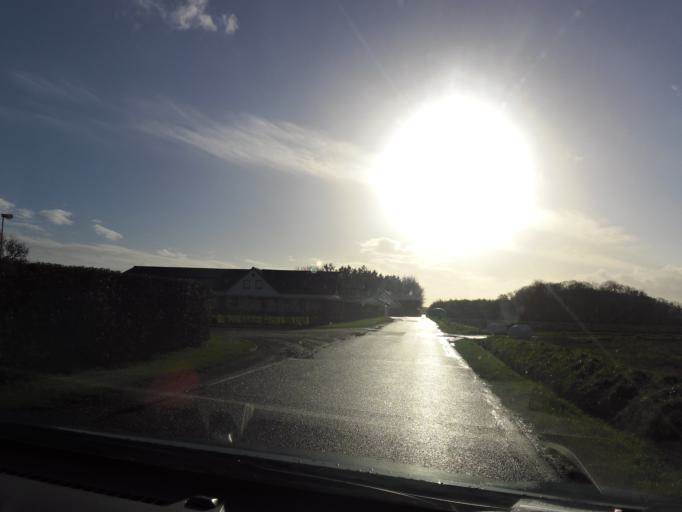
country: DK
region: Central Jutland
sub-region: Odder Kommune
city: Odder
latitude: 55.8735
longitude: 10.1696
